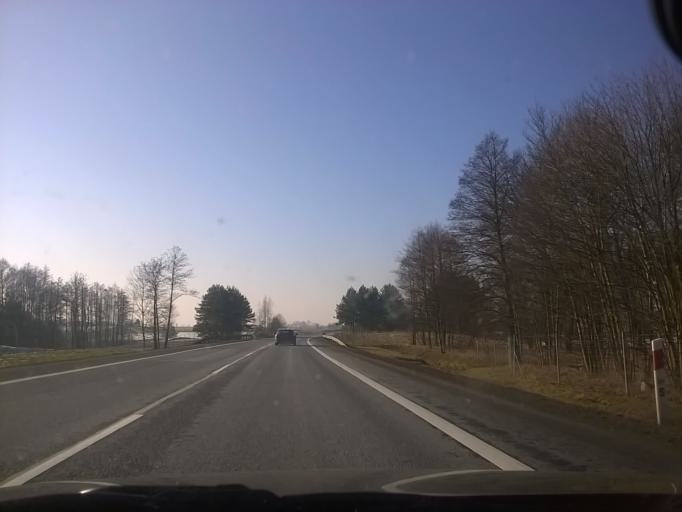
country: PL
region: Warmian-Masurian Voivodeship
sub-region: Powiat olsztynski
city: Barczewo
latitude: 53.8395
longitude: 20.7210
